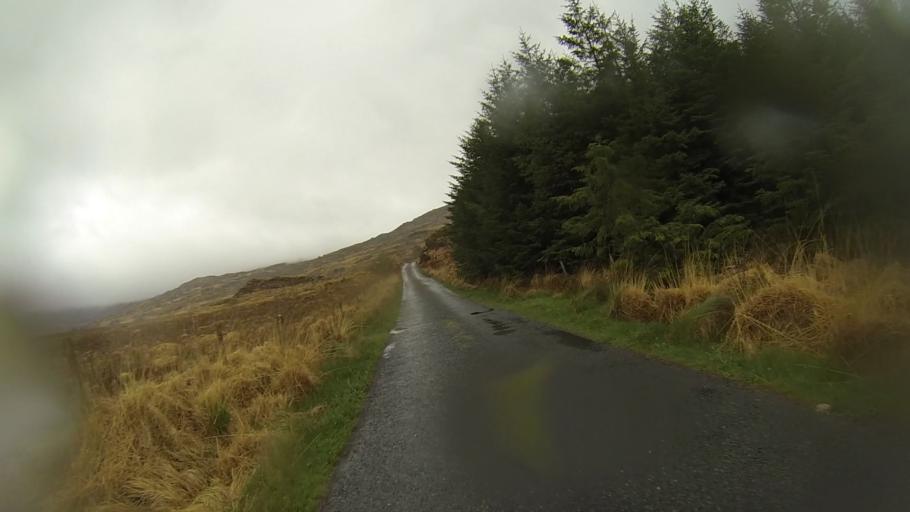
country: IE
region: Munster
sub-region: Ciarrai
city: Kenmare
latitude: 51.9465
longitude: -9.6863
